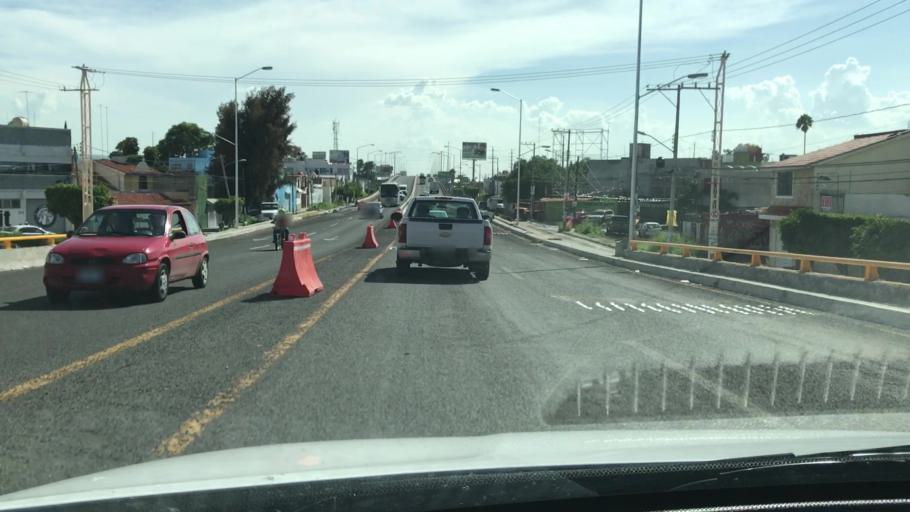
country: MX
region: Guanajuato
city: Celaya
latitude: 20.5154
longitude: -100.7961
